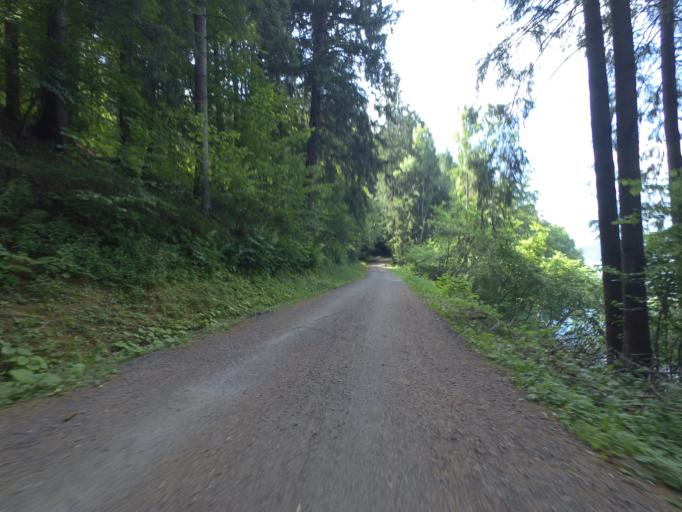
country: AT
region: Carinthia
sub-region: Politischer Bezirk Villach Land
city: Ferndorf
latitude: 46.7673
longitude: 13.6195
